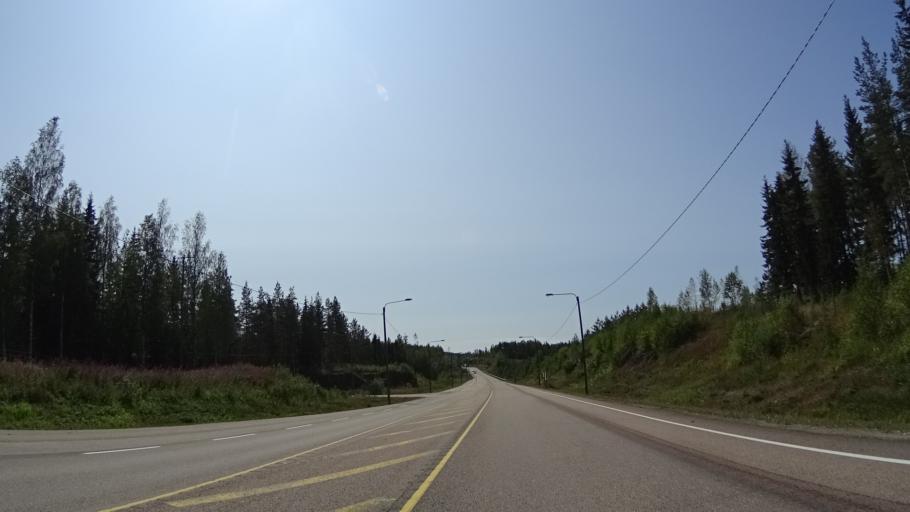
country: FI
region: Central Finland
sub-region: Jaemsae
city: Jaemsae
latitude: 61.7760
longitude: 24.8914
